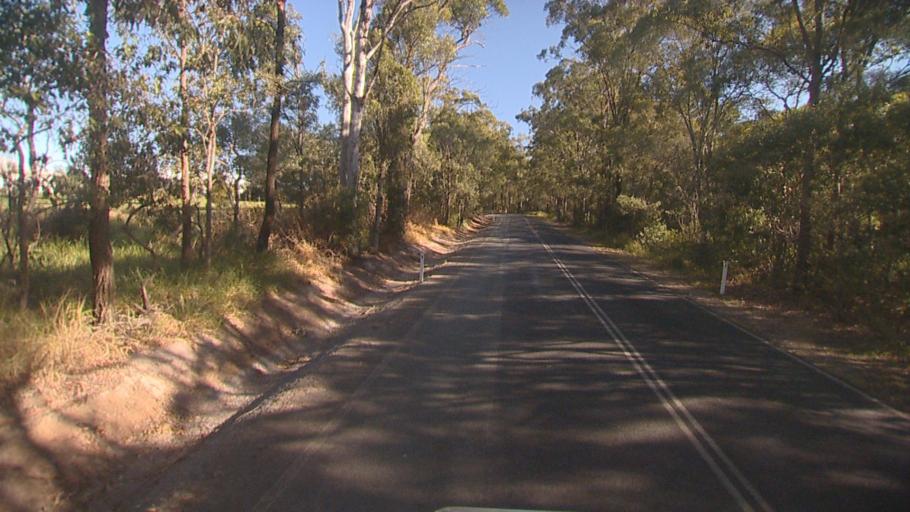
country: AU
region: Queensland
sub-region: Logan
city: Logan Reserve
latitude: -27.7480
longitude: 153.1324
